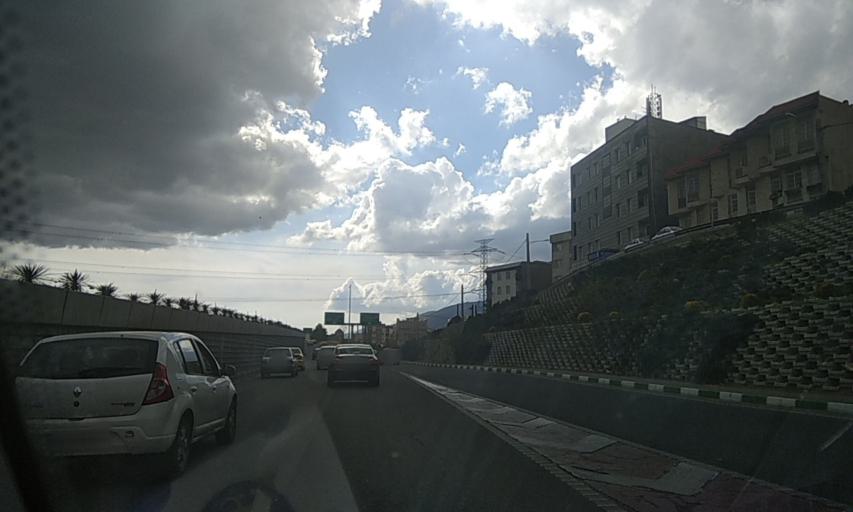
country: IR
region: Tehran
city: Tajrish
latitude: 35.7707
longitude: 51.3211
